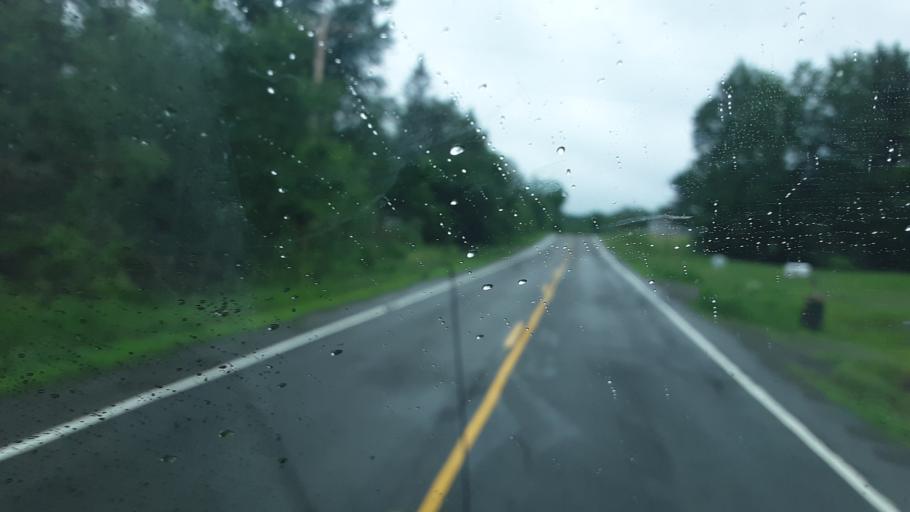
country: US
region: Maine
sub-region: Penobscot County
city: Patten
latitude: 46.0562
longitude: -68.4412
